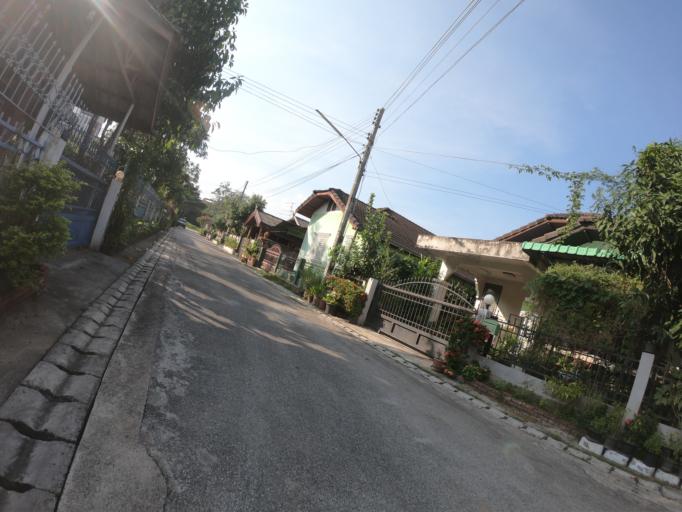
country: TH
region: Chiang Mai
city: San Sai
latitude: 18.8202
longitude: 99.0142
